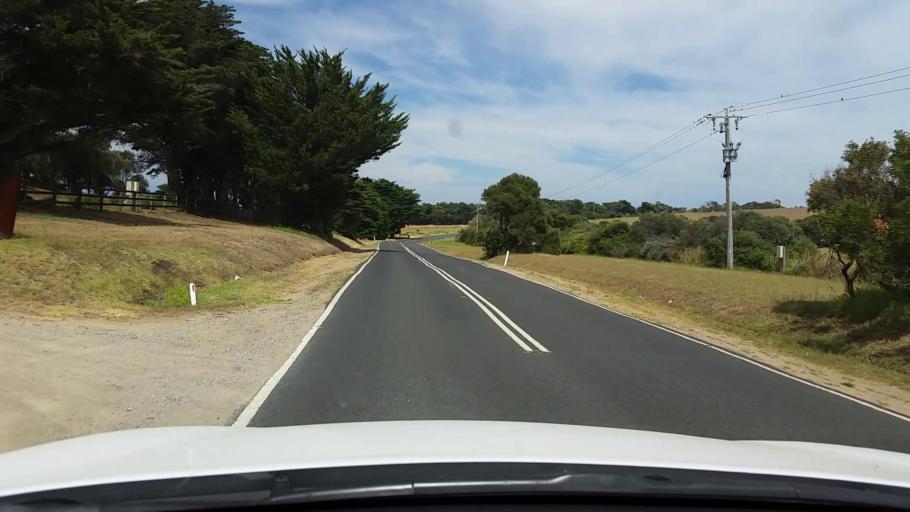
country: AU
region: Victoria
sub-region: Mornington Peninsula
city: Merricks
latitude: -38.4775
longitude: 144.9935
